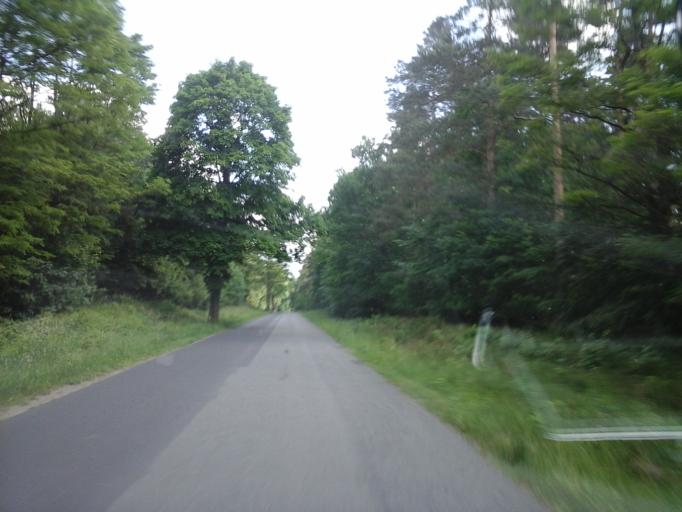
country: PL
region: Lubusz
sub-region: Powiat strzelecko-drezdenecki
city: Dobiegniew
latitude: 53.0616
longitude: 15.7624
